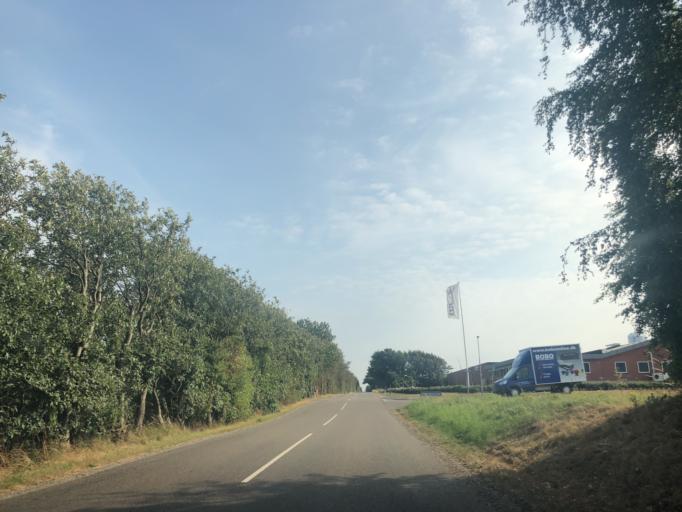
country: DK
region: Central Jutland
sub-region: Skive Kommune
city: Skive
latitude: 56.6967
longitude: 8.9789
